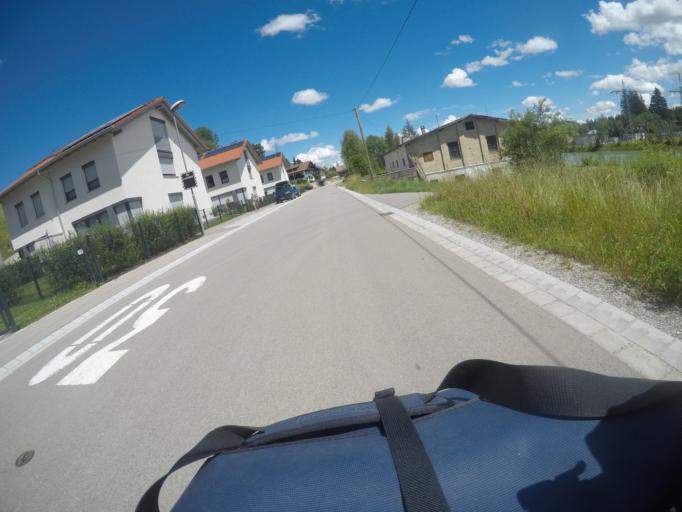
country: DE
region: Bavaria
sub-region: Upper Bavaria
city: Prem
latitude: 47.6914
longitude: 10.7957
